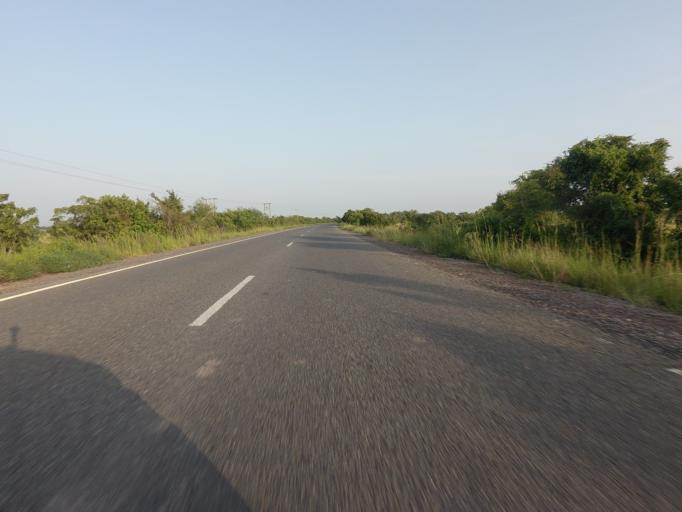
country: GH
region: Volta
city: Anloga
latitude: 5.9143
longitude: 0.7079
